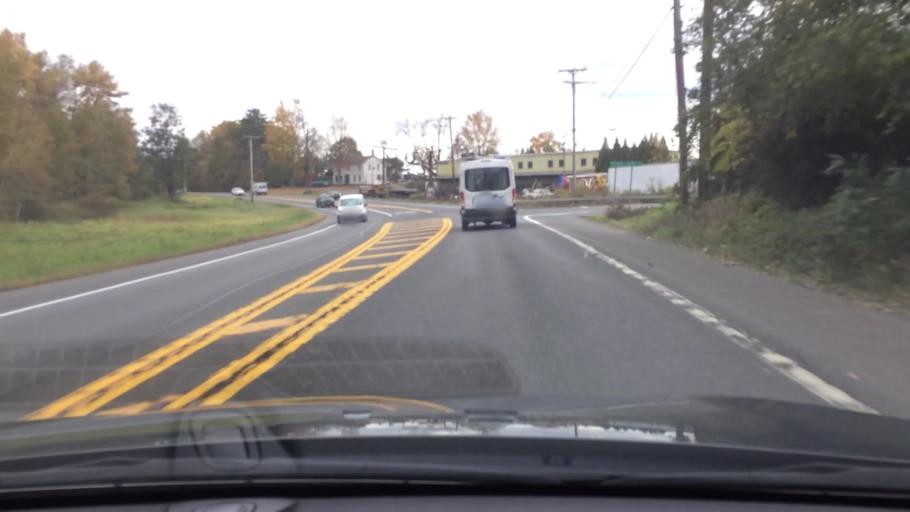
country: US
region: New York
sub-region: Columbia County
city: Niverville
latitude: 42.4700
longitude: -73.6896
